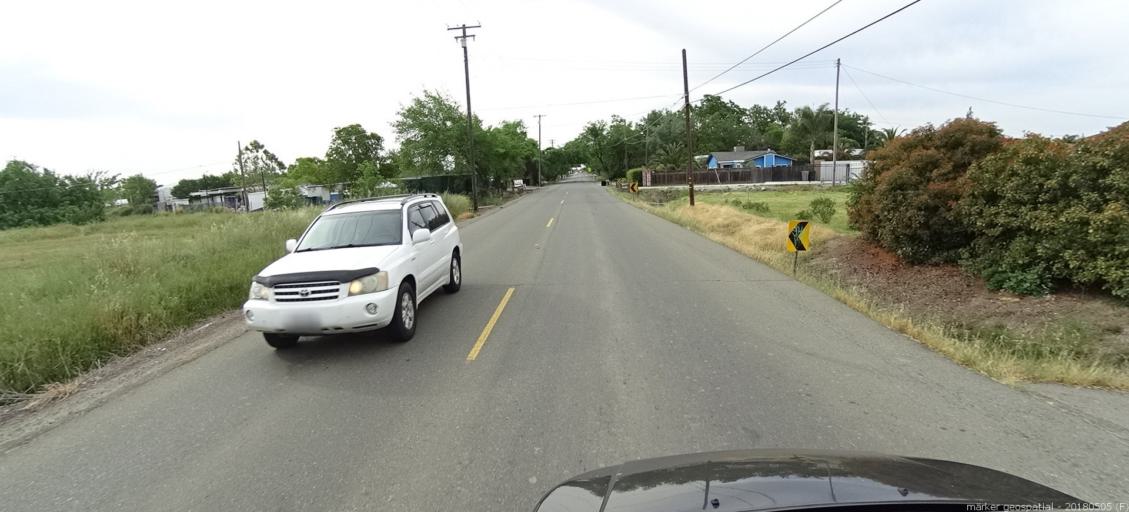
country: US
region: California
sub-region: Sacramento County
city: Rio Linda
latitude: 38.6569
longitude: -121.4427
